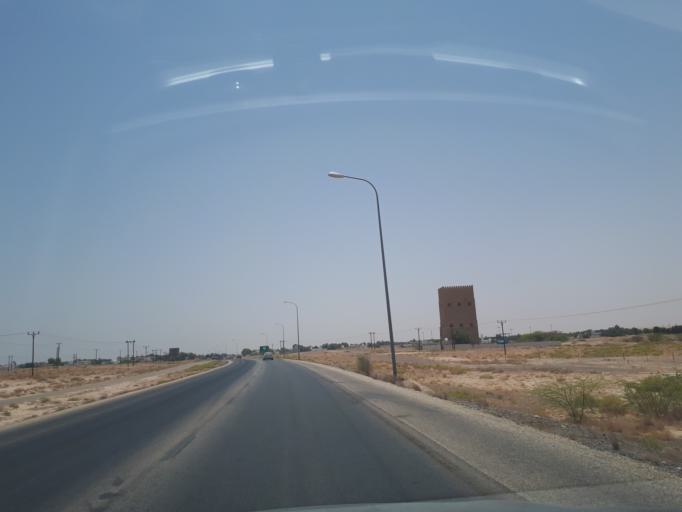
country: OM
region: Ash Sharqiyah
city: Al Qabil
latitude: 22.5104
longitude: 58.7403
